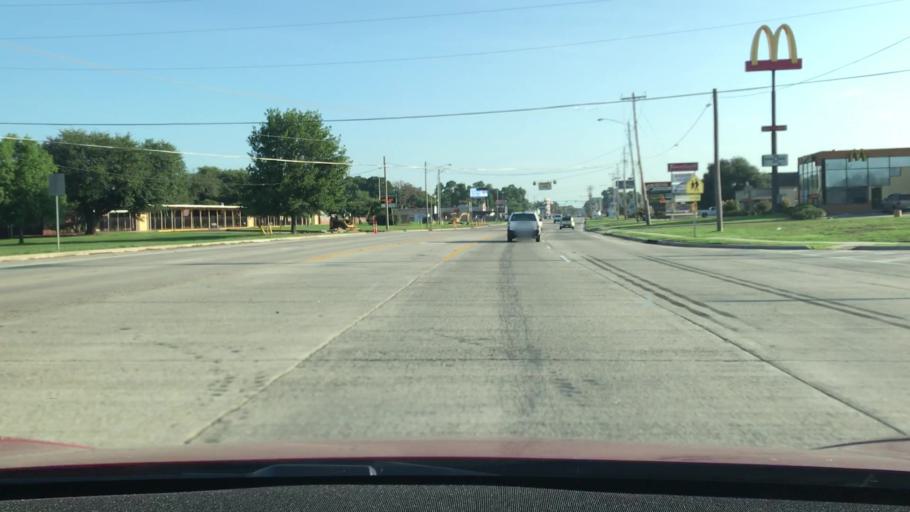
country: US
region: Louisiana
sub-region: Bossier Parish
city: Bossier City
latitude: 32.4506
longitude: -93.7220
